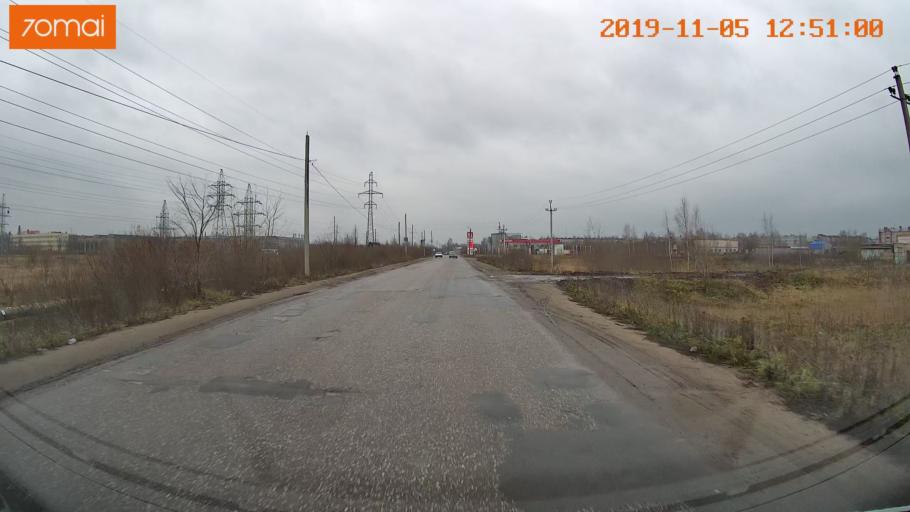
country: RU
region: Ivanovo
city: Kokhma
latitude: 56.9470
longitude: 41.1101
